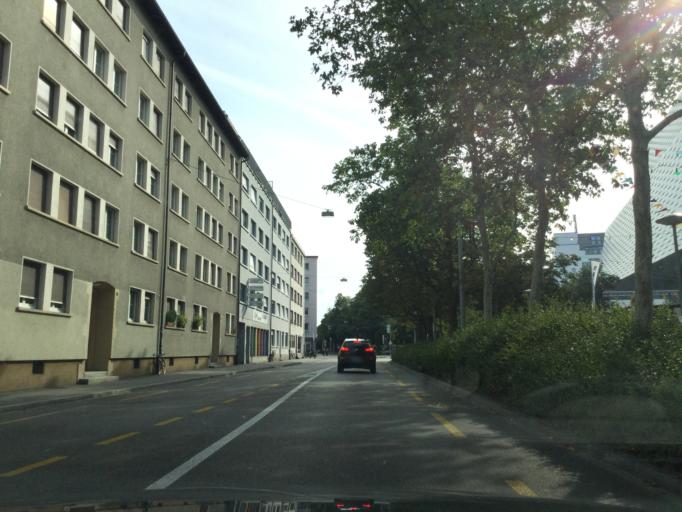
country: CH
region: Basel-Landschaft
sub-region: Bezirk Arlesheim
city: Birsfelden
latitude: 47.5628
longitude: 7.6014
